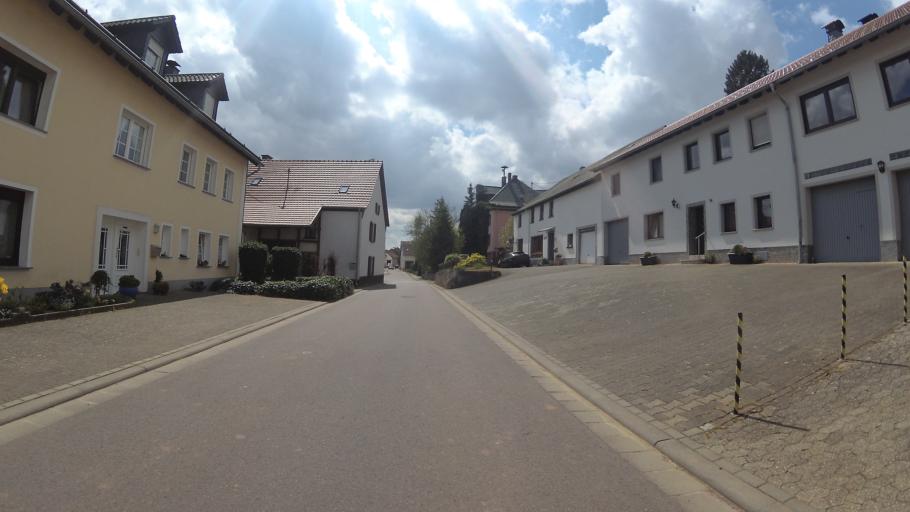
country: DE
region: Saarland
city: Nonnweiler
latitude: 49.5754
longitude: 6.9263
